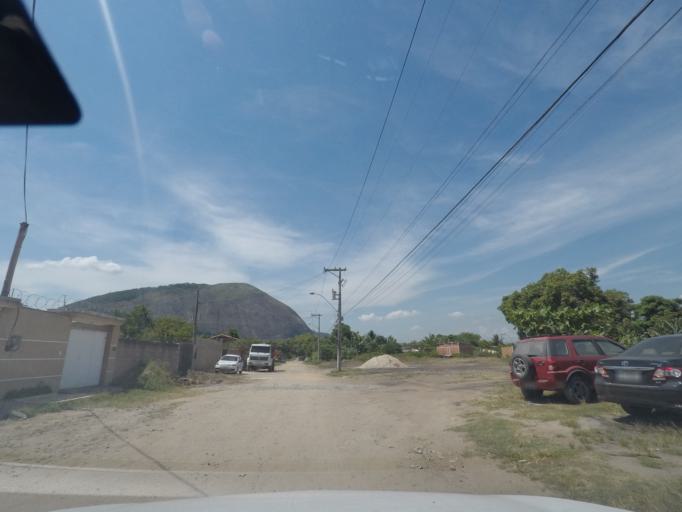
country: BR
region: Rio de Janeiro
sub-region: Marica
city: Marica
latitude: -22.9539
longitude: -42.9586
